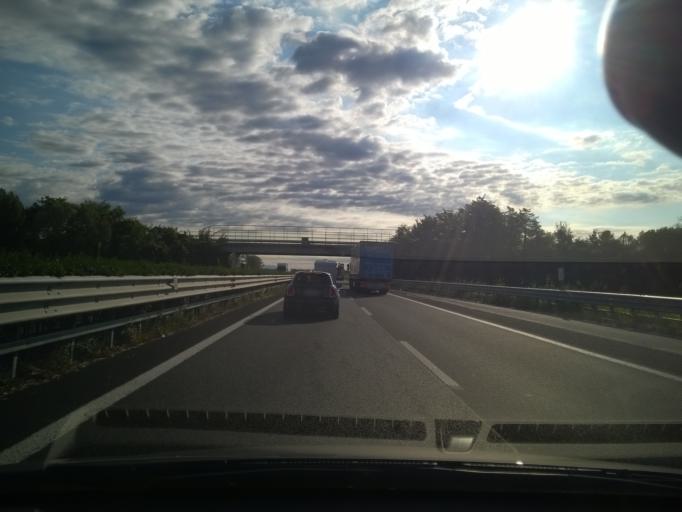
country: IT
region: Veneto
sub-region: Provincia di Venezia
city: San Giorgio al Tagliamento-Pozzi
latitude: 45.8072
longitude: 12.9389
